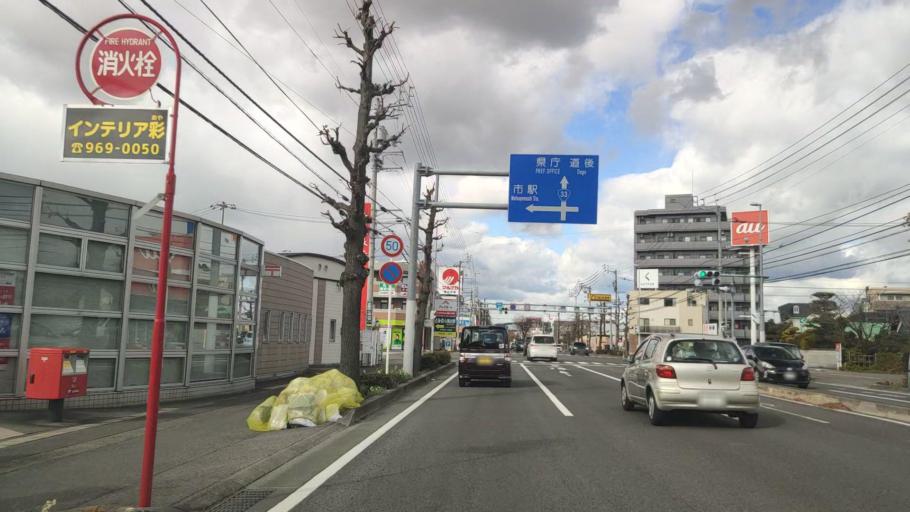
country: JP
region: Ehime
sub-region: Shikoku-chuo Shi
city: Matsuyama
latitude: 33.8113
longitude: 132.7791
